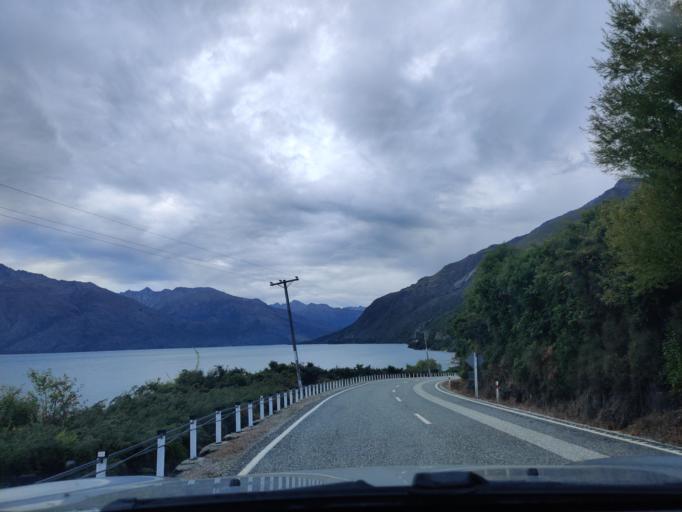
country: NZ
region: Otago
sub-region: Queenstown-Lakes District
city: Wanaka
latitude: -44.4021
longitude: 169.1868
